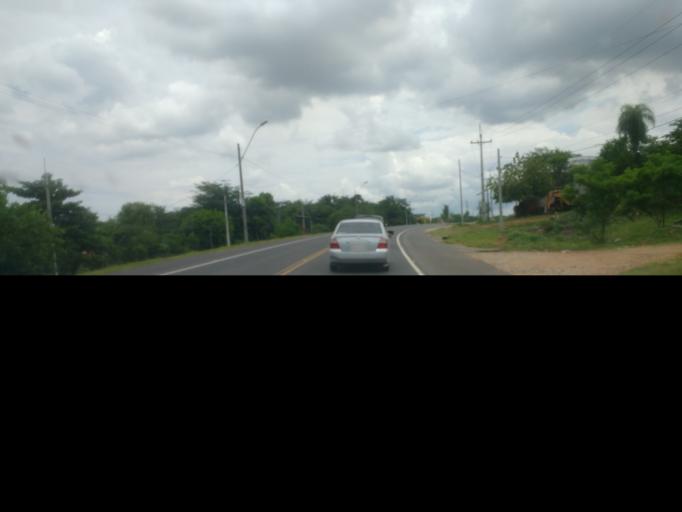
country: PY
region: Central
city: Limpio
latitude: -25.1342
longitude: -57.4484
